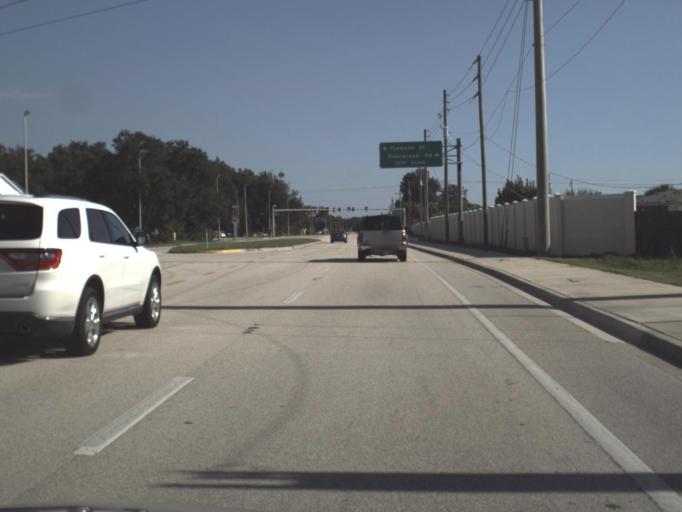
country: US
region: Florida
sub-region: Sarasota County
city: Englewood
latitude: 27.0069
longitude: -82.3807
